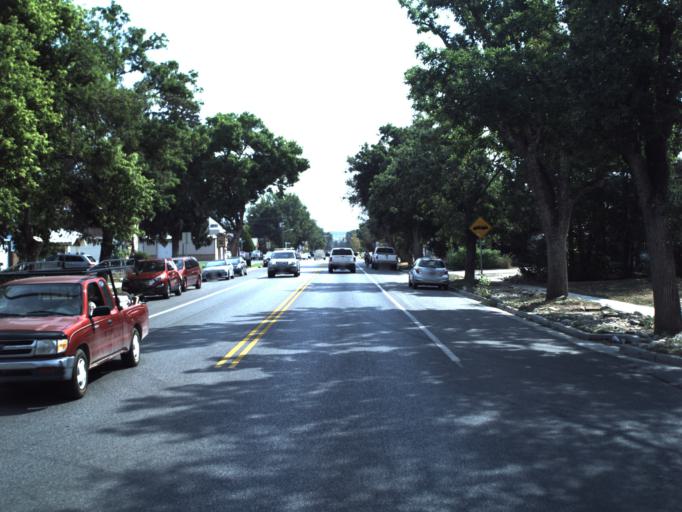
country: US
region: Utah
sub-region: Wasatch County
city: Heber
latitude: 40.5064
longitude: -111.4170
